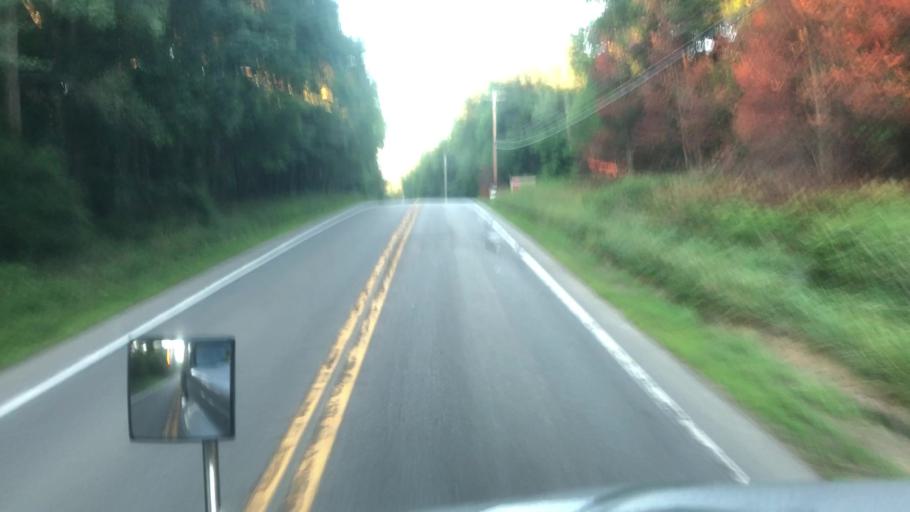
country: US
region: Pennsylvania
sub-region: Venango County
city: Hasson Heights
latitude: 41.5222
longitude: -79.6163
